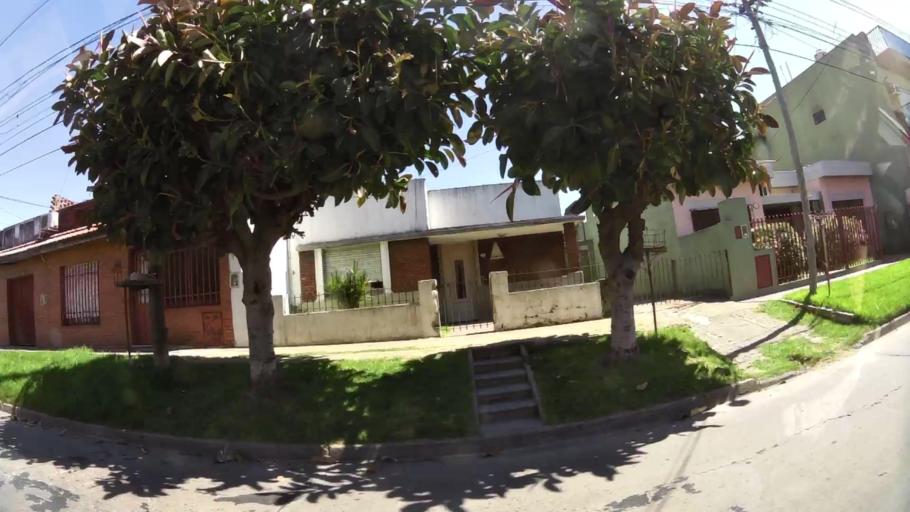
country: AR
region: Buenos Aires
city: Caseros
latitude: -34.5678
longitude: -58.5706
